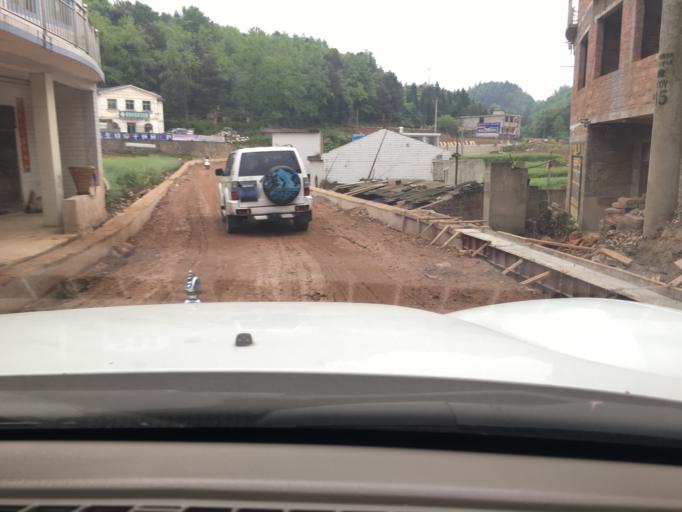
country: CN
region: Guizhou Sheng
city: Supu
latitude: 26.7301
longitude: 106.4374
